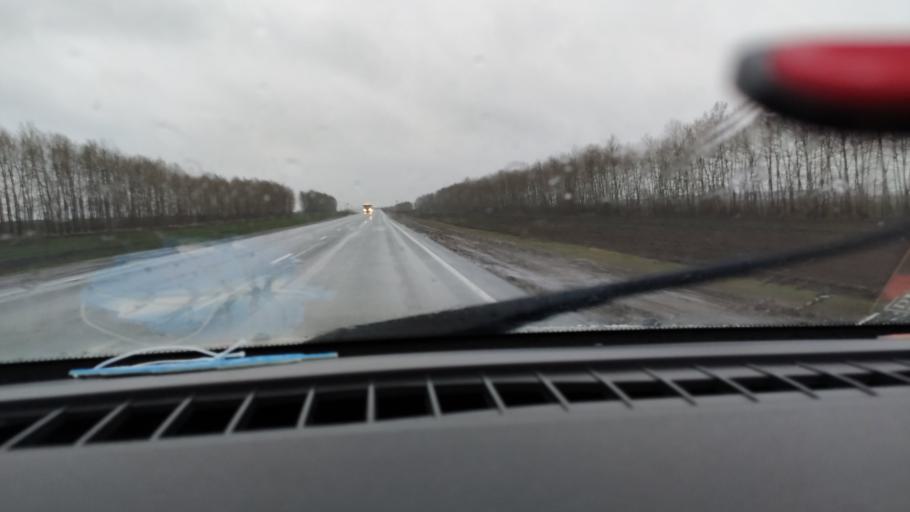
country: RU
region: Tatarstan
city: Mendeleyevsk
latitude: 55.9292
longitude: 52.2805
